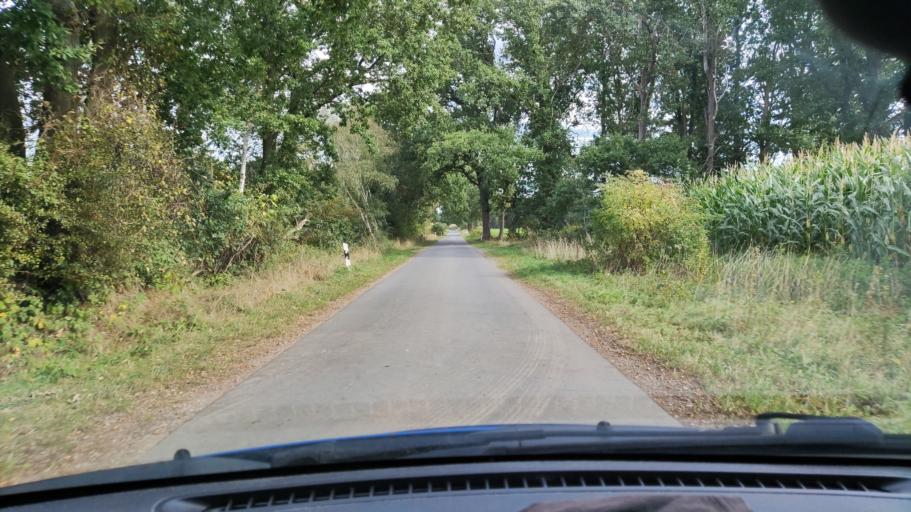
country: DE
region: Lower Saxony
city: Himbergen
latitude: 53.1082
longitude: 10.6922
